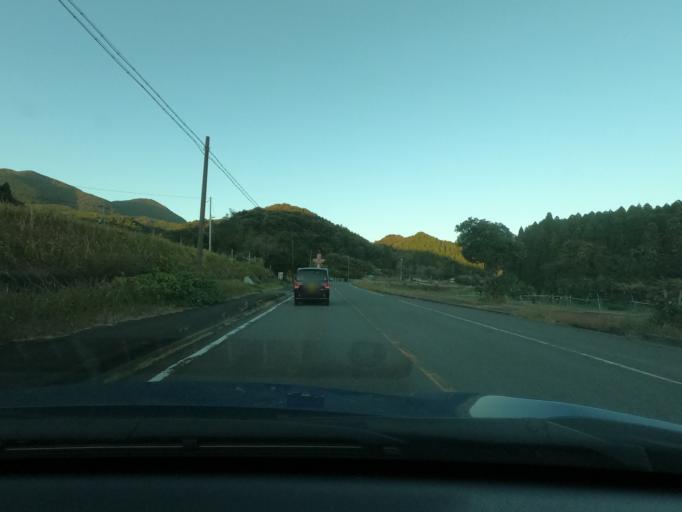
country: JP
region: Kagoshima
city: Satsumasendai
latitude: 31.7948
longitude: 130.4727
